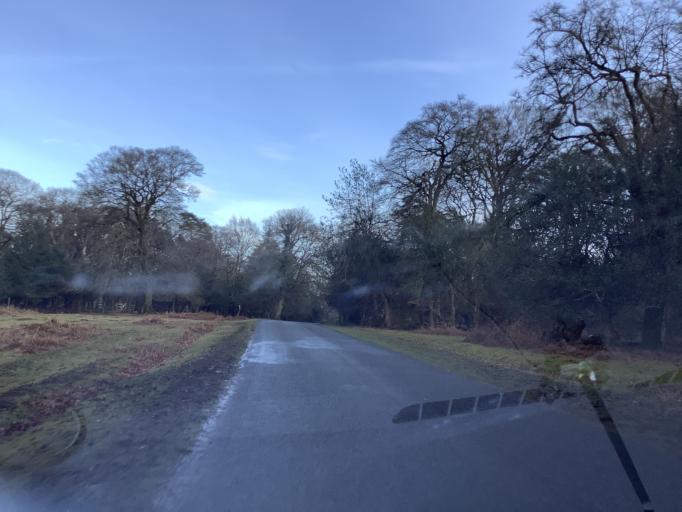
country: GB
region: England
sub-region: Hampshire
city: Lyndhurst
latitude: 50.8738
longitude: -1.6520
